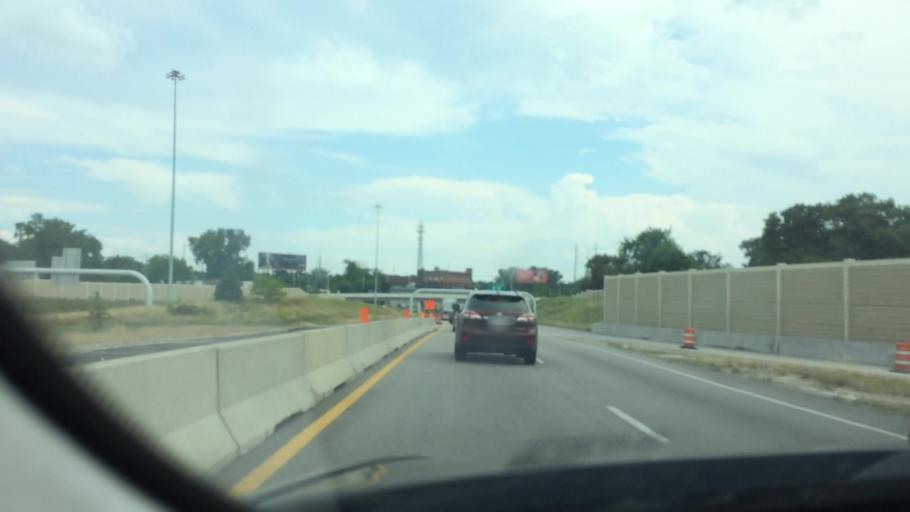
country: US
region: Ohio
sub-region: Lucas County
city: Toledo
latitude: 41.6736
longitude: -83.5737
